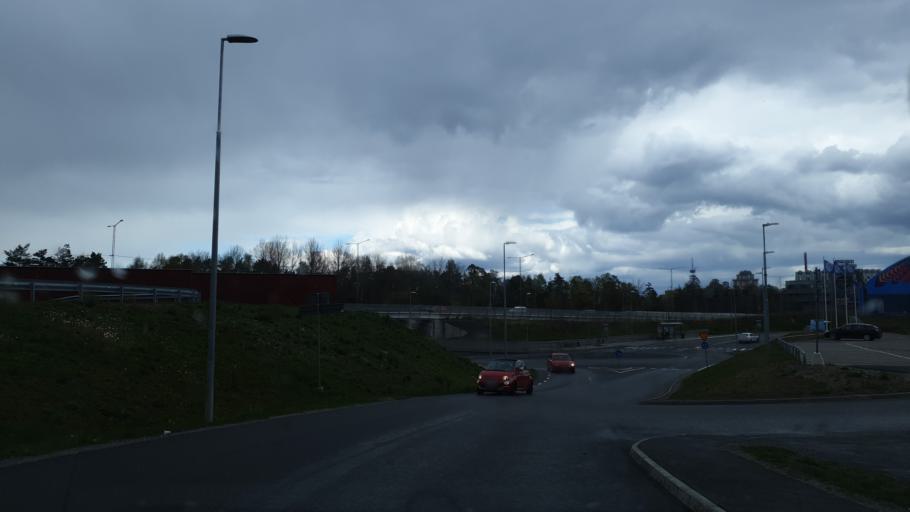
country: SE
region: Stockholm
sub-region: Nacka Kommun
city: Nacka
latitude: 59.3112
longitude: 18.1524
